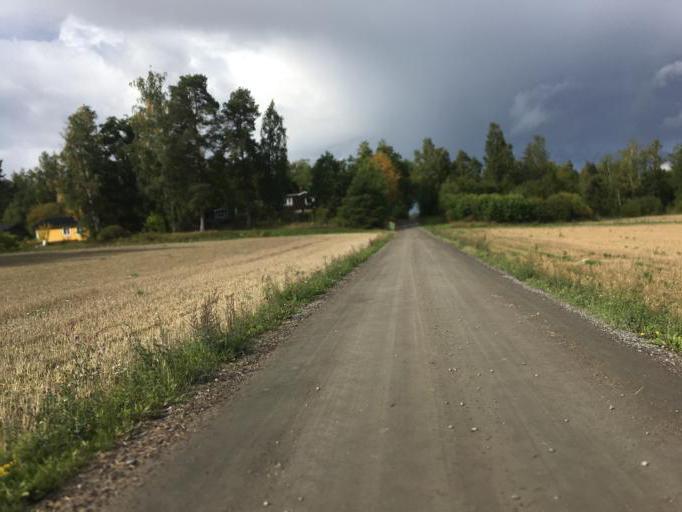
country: SE
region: Soedermanland
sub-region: Eskilstuna Kommun
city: Eskilstuna
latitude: 59.4507
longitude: 16.6472
